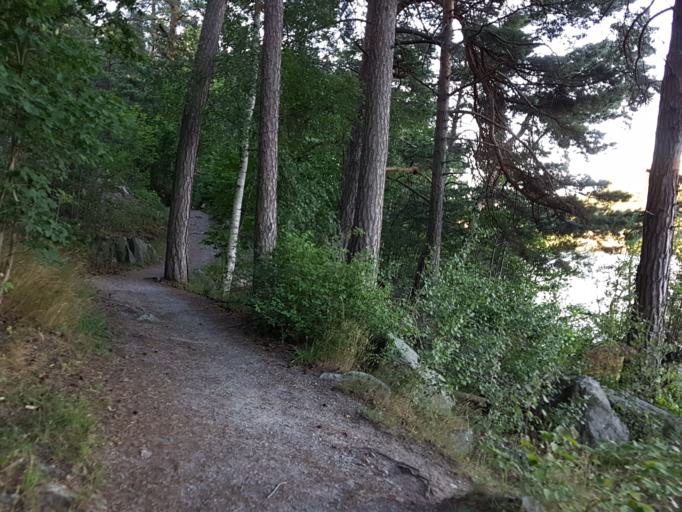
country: SE
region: Stockholm
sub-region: Sundbybergs Kommun
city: Sundbyberg
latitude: 59.3209
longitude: 17.9767
